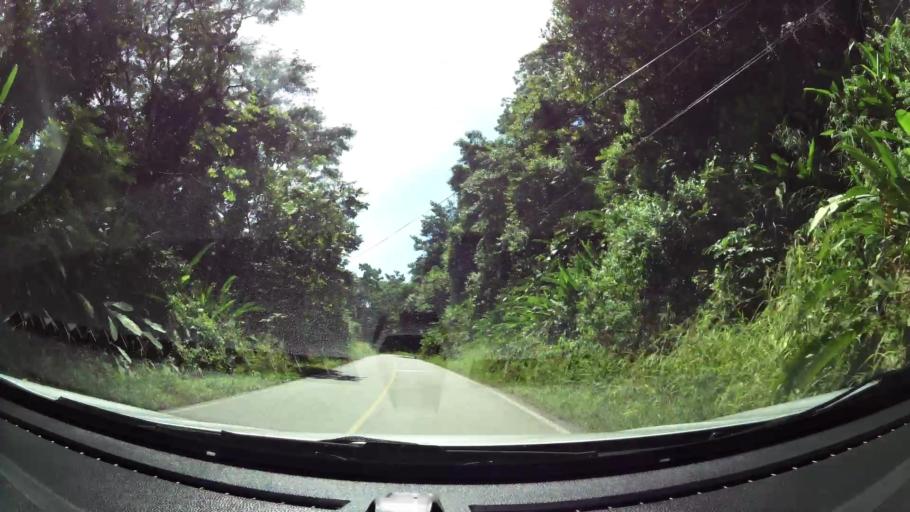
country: CR
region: San Jose
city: San Isidro
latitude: 9.2629
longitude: -83.8627
